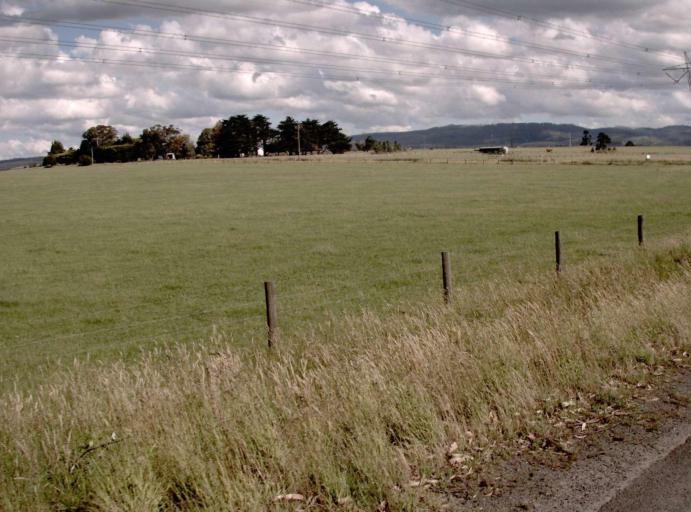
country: AU
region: Victoria
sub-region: Latrobe
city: Morwell
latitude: -38.2654
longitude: 146.4347
